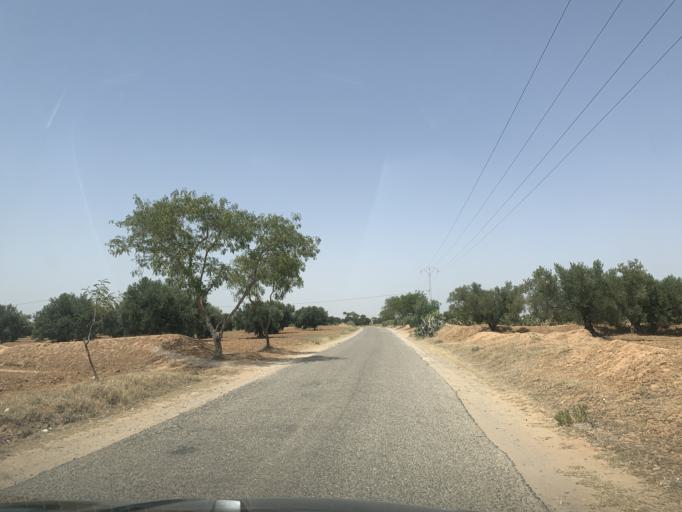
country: TN
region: Al Mahdiyah
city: Shurban
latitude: 35.1855
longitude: 10.2425
